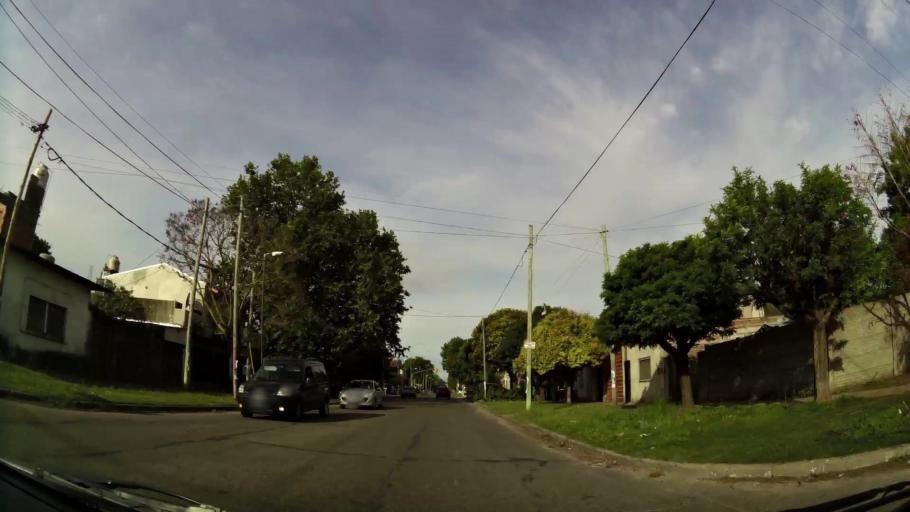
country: AR
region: Buenos Aires
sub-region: Partido de Quilmes
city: Quilmes
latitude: -34.7417
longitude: -58.2598
